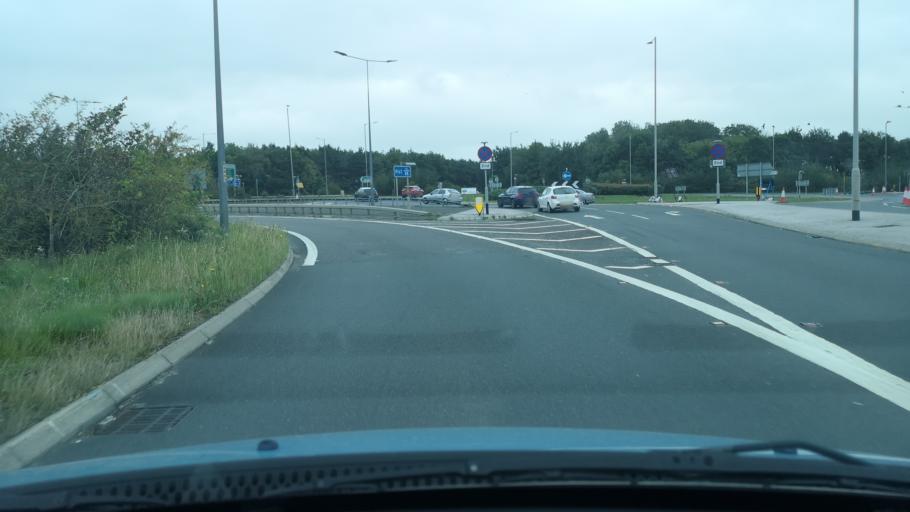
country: GB
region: England
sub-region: East Riding of Yorkshire
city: Airmyn
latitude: 53.7043
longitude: -0.9089
